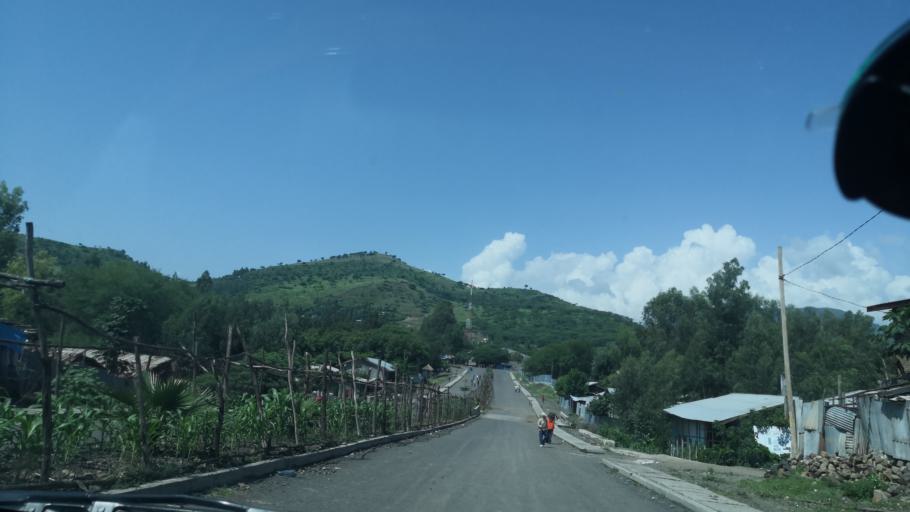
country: ET
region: Amhara
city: Abomsa
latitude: 10.3398
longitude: 39.9601
